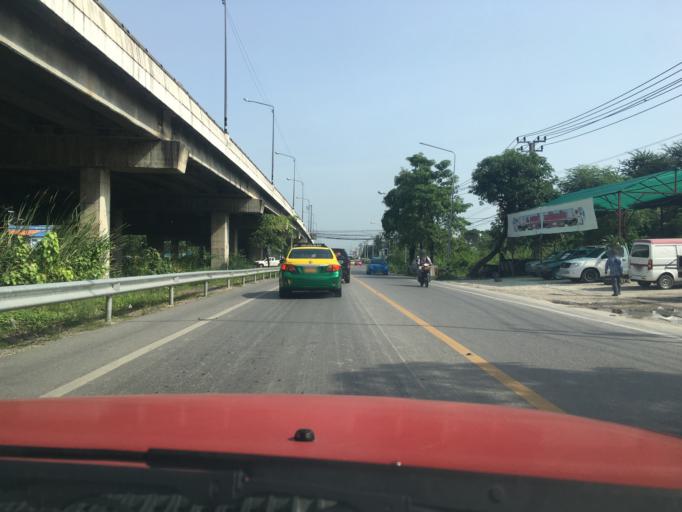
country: TH
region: Bangkok
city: Bang Bon
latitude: 13.6341
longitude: 100.4155
